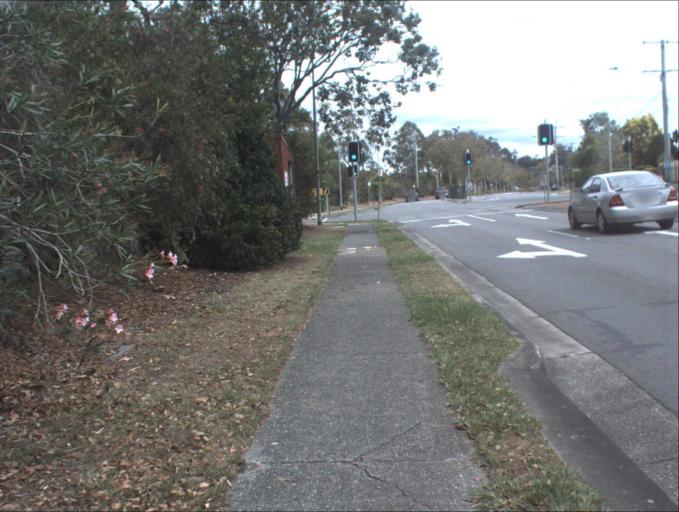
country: AU
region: Queensland
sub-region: Logan
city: Slacks Creek
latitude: -27.6596
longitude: 153.1738
